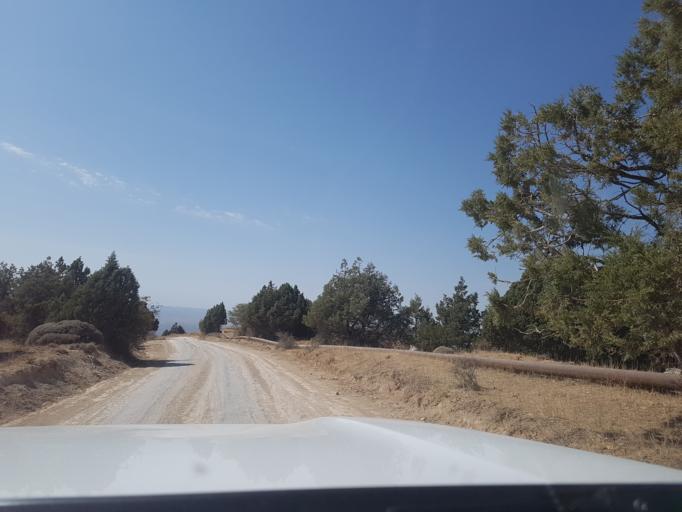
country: TM
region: Ahal
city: Baharly
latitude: 38.3137
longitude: 56.9516
